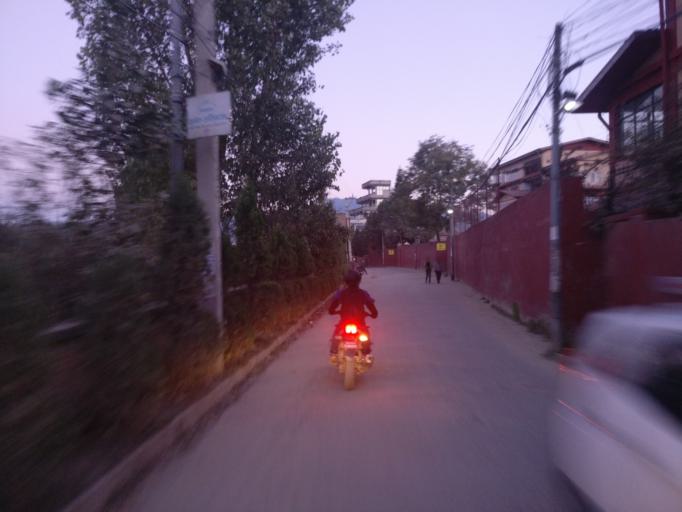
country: NP
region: Central Region
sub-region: Bagmati Zone
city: Patan
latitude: 27.6503
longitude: 85.3219
